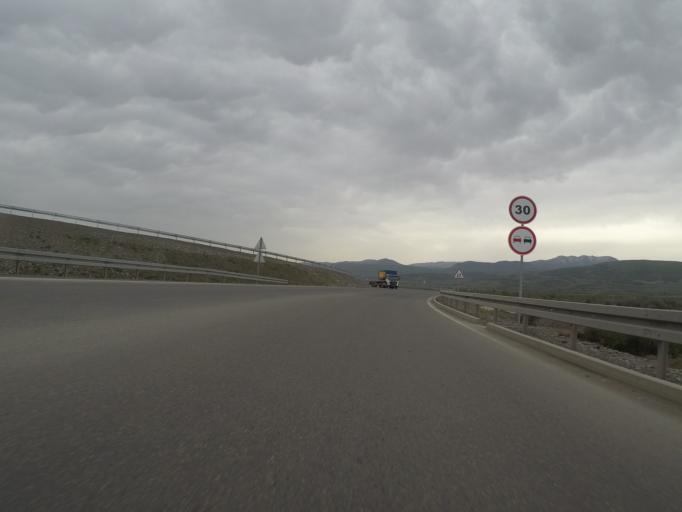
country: GE
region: Shida Kartli
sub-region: Khashuris Raioni
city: Khashuri
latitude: 42.0104
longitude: 43.6979
